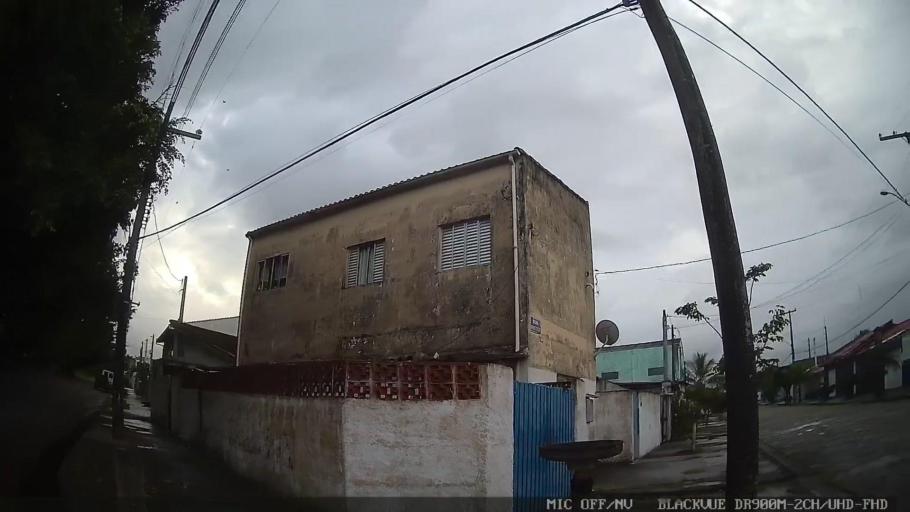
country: BR
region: Sao Paulo
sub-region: Itanhaem
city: Itanhaem
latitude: -24.1782
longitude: -46.7807
